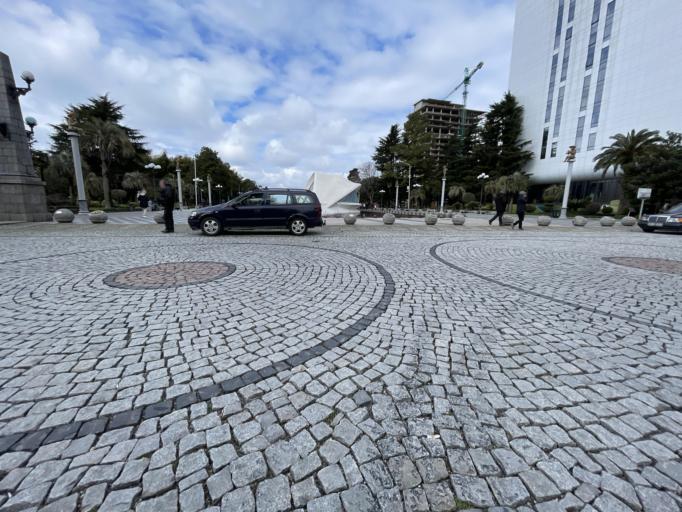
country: GE
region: Ajaria
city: Batumi
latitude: 41.6534
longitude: 41.6358
